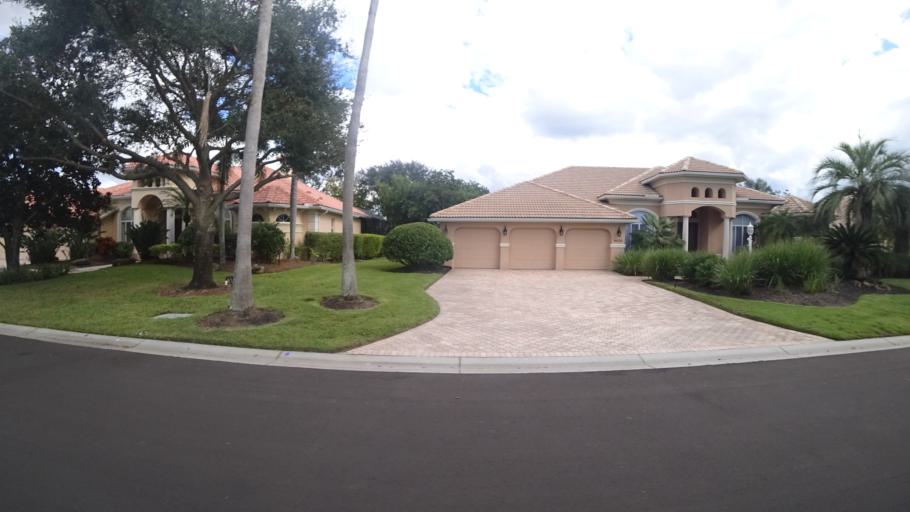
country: US
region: Florida
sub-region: Sarasota County
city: The Meadows
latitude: 27.3954
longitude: -82.4172
